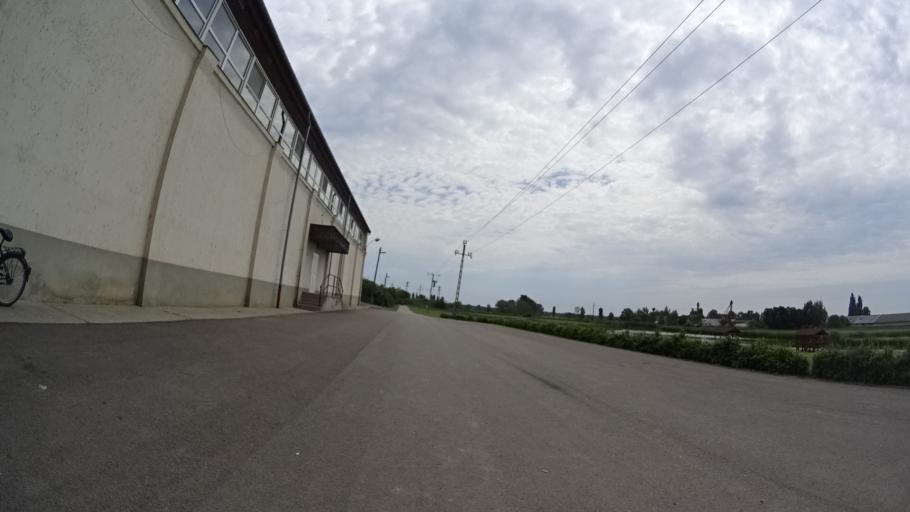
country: HU
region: Bacs-Kiskun
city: Tiszakecske
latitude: 46.9265
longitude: 20.1140
